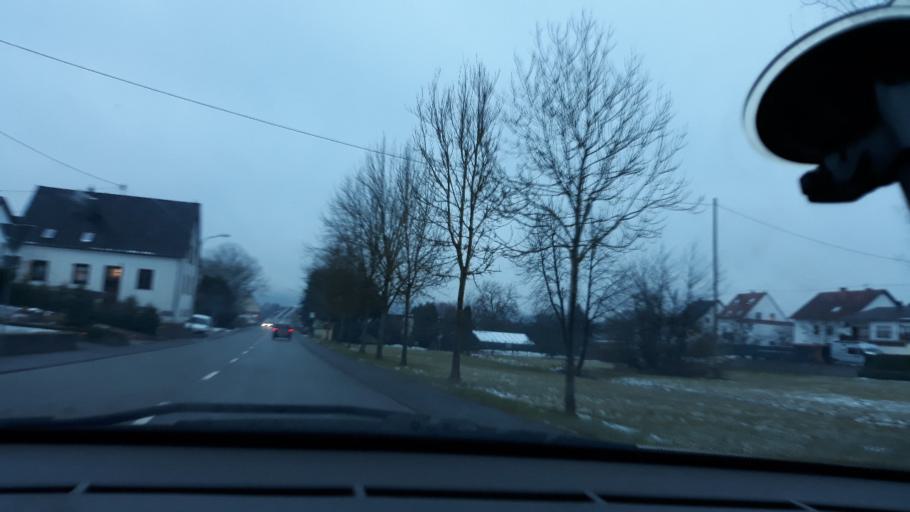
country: DE
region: Saarland
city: Gersheim
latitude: 49.2019
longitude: 7.1738
